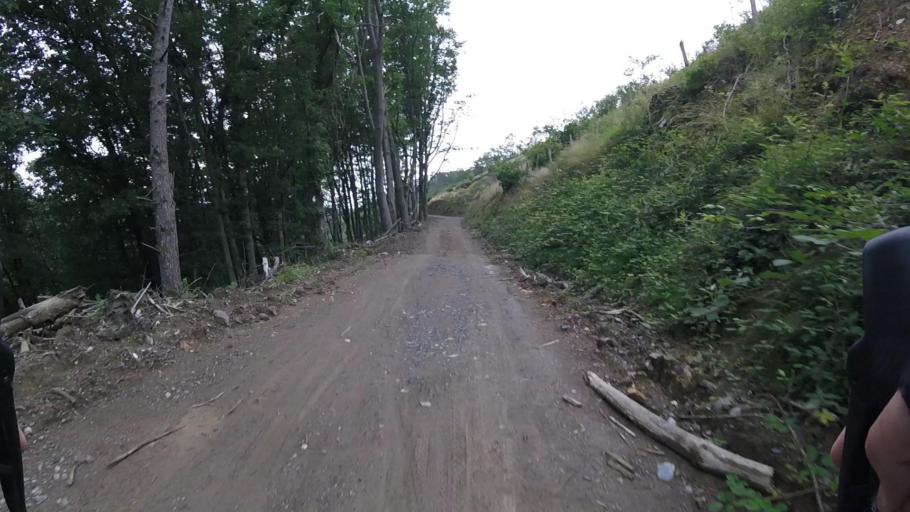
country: ES
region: Navarre
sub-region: Provincia de Navarra
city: Arano
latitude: 43.2533
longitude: -1.8576
